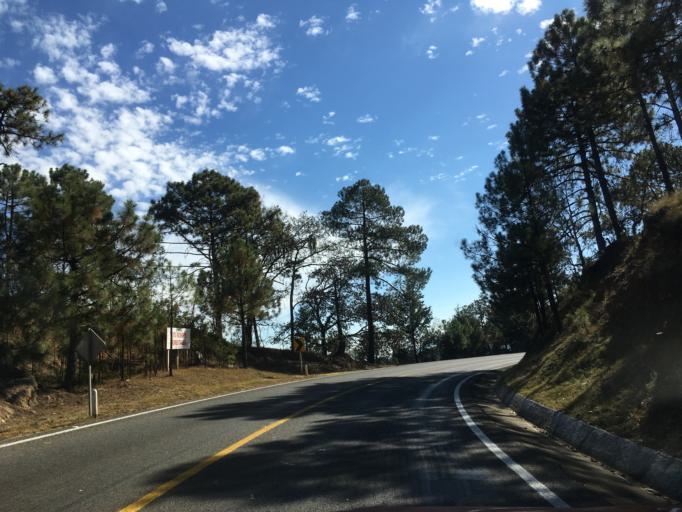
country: MX
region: Michoacan
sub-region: Hidalgo
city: Tierras Coloradas (San Pedro)
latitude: 19.6732
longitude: -100.7237
